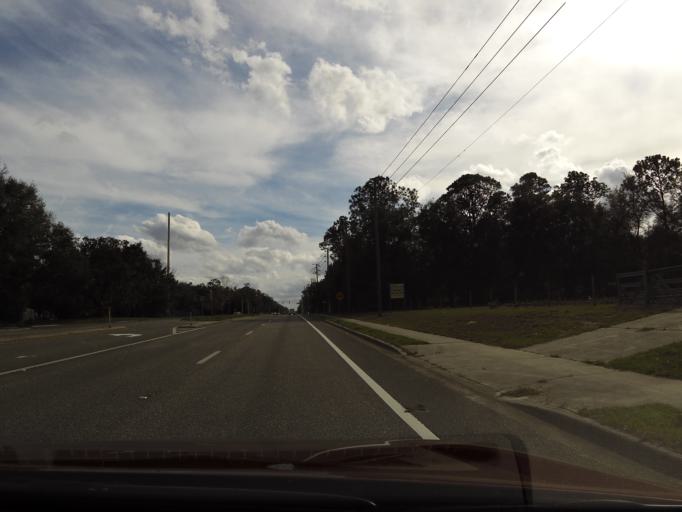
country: US
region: Florida
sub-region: Volusia County
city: North DeLand
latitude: 29.0743
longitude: -81.3255
